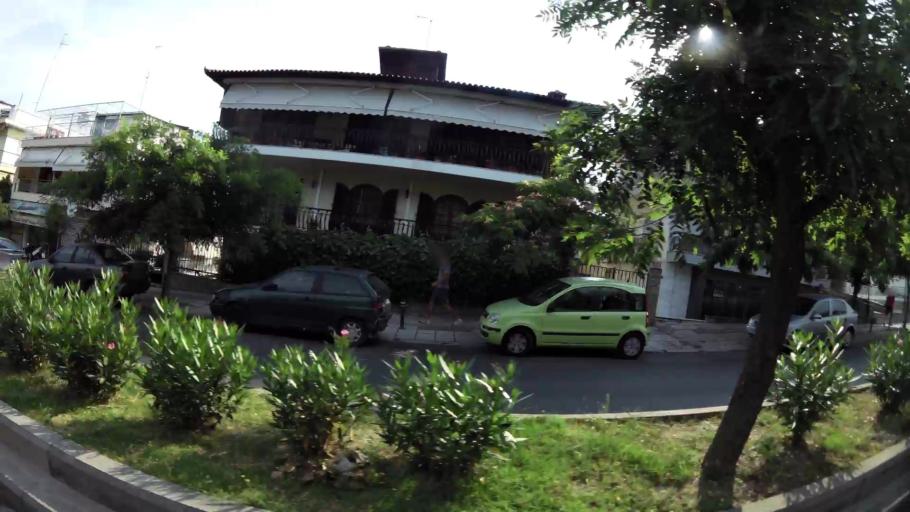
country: GR
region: Central Macedonia
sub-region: Nomos Thessalonikis
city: Sykies
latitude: 40.6494
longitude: 22.9594
